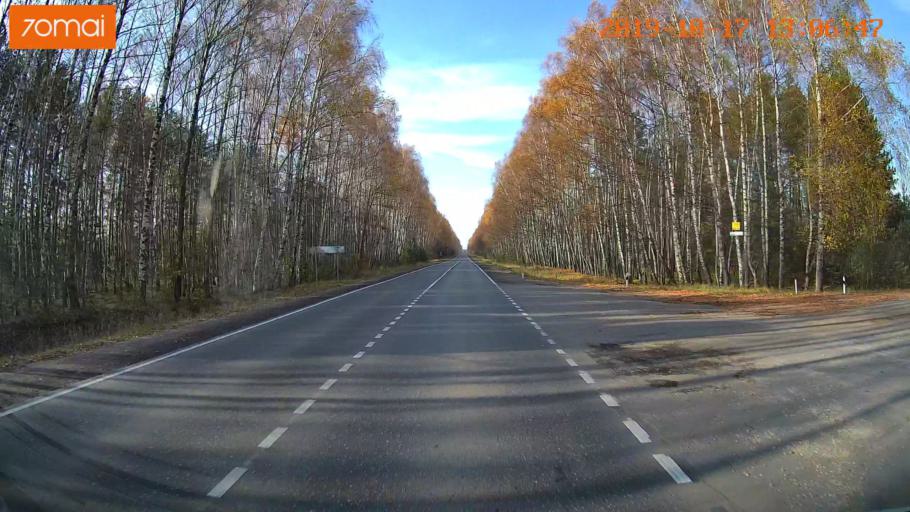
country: RU
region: Rjazan
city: Syntul
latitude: 54.9775
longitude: 41.3062
